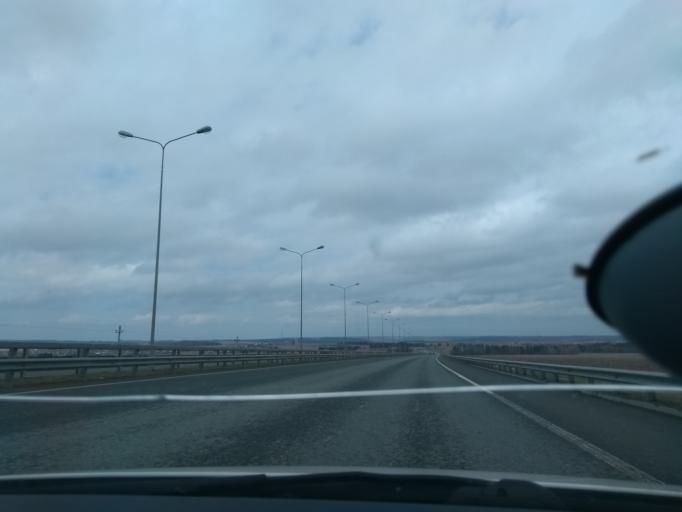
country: RU
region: Perm
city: Zvezdnyy
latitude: 57.7681
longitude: 56.3351
